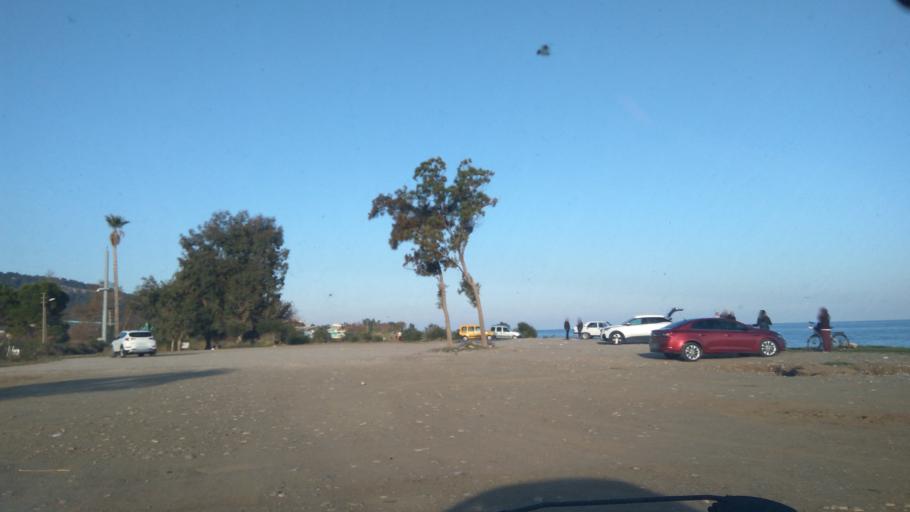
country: TR
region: Antalya
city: Kemer
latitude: 36.5599
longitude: 30.5720
